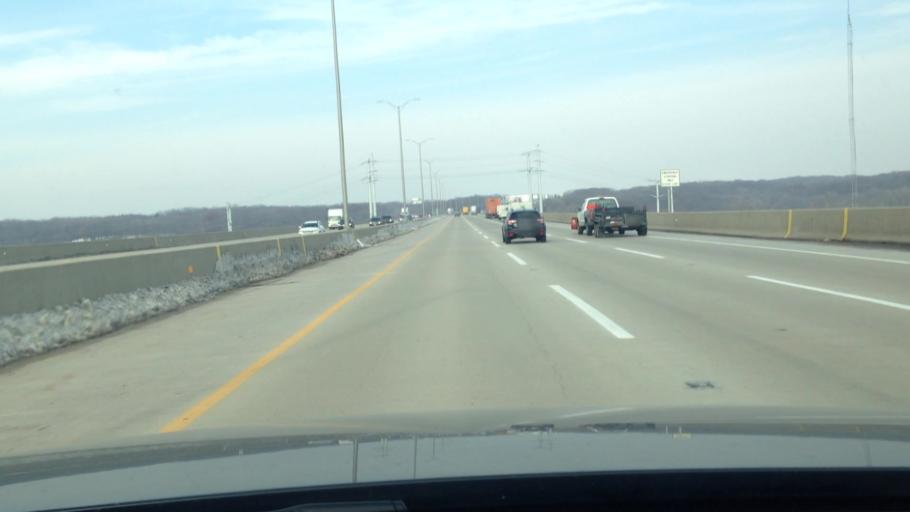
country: US
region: Illinois
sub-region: Cook County
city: Lemont
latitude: 41.6708
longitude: -88.0286
